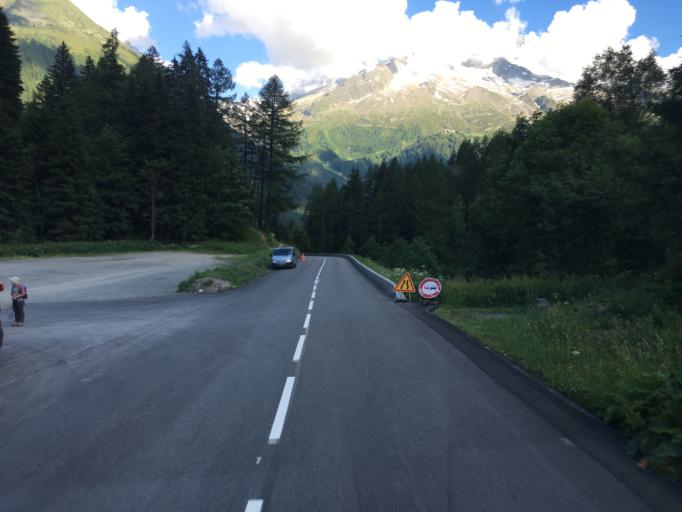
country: FR
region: Rhone-Alpes
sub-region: Departement de la Haute-Savoie
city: Chamonix-Mont-Blanc
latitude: 45.9993
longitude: 6.9236
